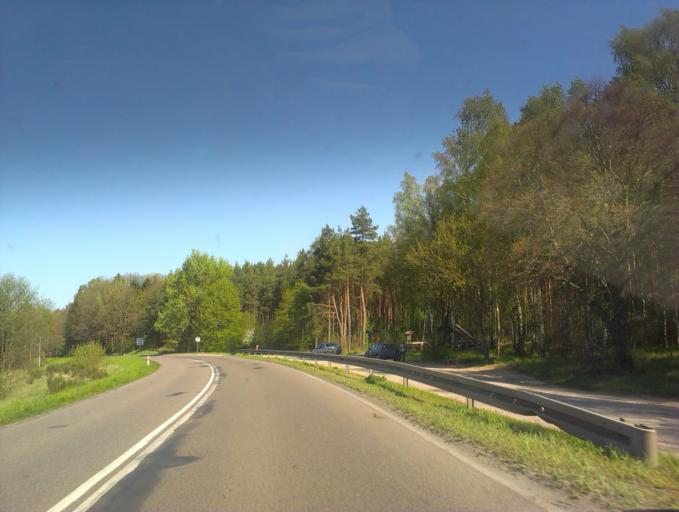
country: PL
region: West Pomeranian Voivodeship
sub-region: Powiat swidwinski
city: Polczyn-Zdroj
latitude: 53.7887
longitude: 16.0722
